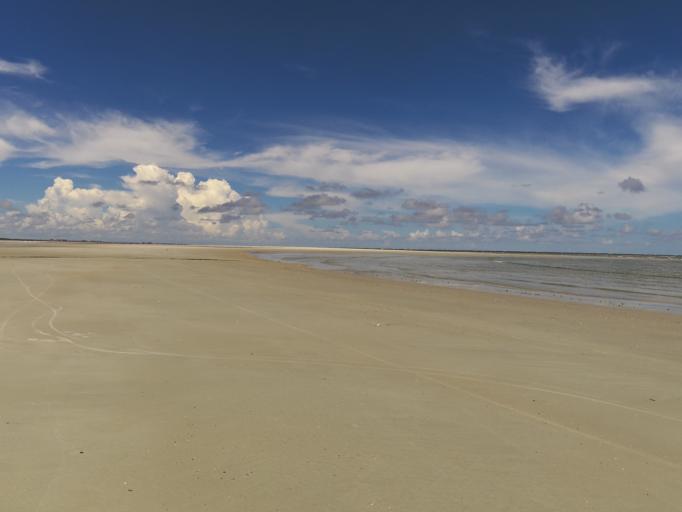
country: US
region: Florida
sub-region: Duval County
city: Atlantic Beach
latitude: 30.4857
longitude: -81.4155
